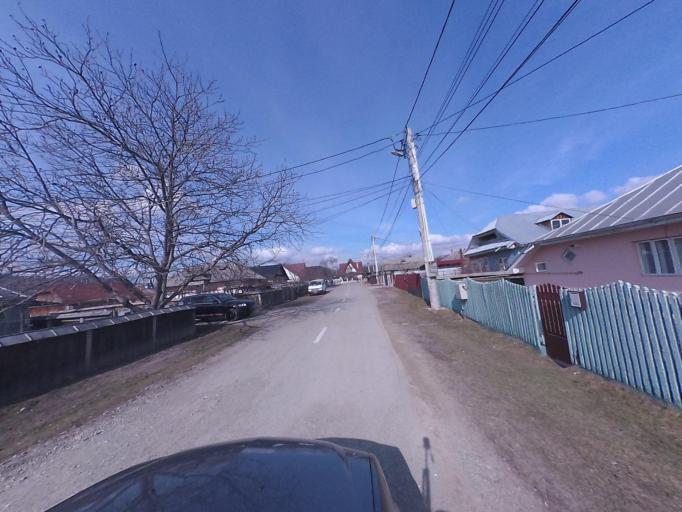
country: RO
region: Neamt
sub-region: Oras Targu Neamt
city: Targu Neamt
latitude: 47.2067
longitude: 26.3837
